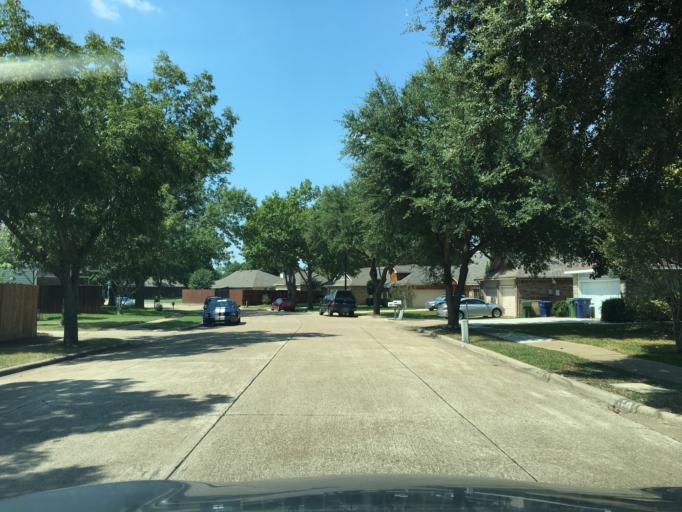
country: US
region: Texas
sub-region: Collin County
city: Plano
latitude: 32.9685
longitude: -96.6662
